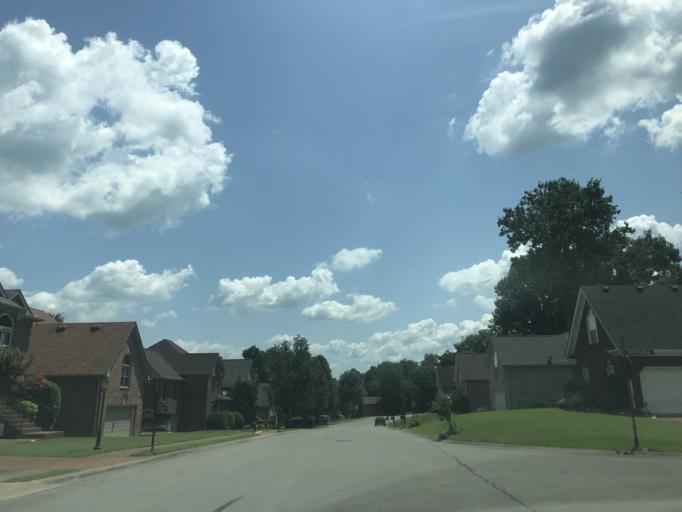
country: US
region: Tennessee
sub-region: Wilson County
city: Green Hill
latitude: 36.1532
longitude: -86.5933
